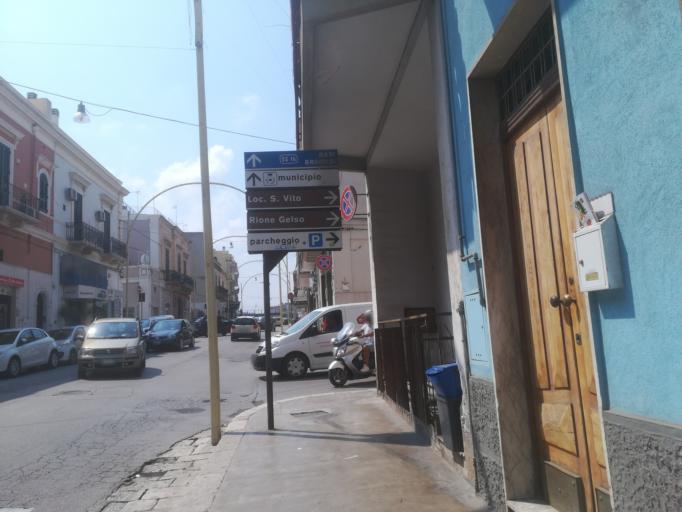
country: IT
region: Apulia
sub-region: Provincia di Bari
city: Polignano a Mare
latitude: 40.9938
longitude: 17.2181
